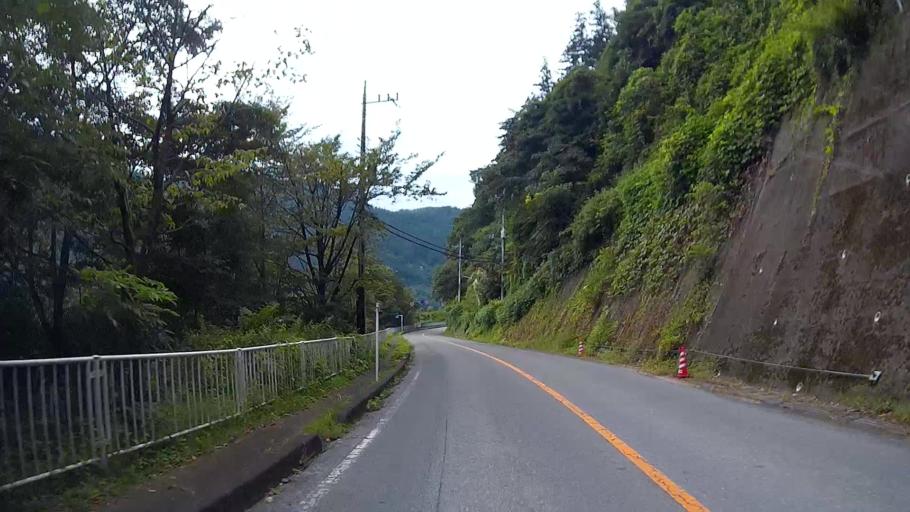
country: JP
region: Saitama
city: Chichibu
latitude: 35.9493
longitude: 139.0569
